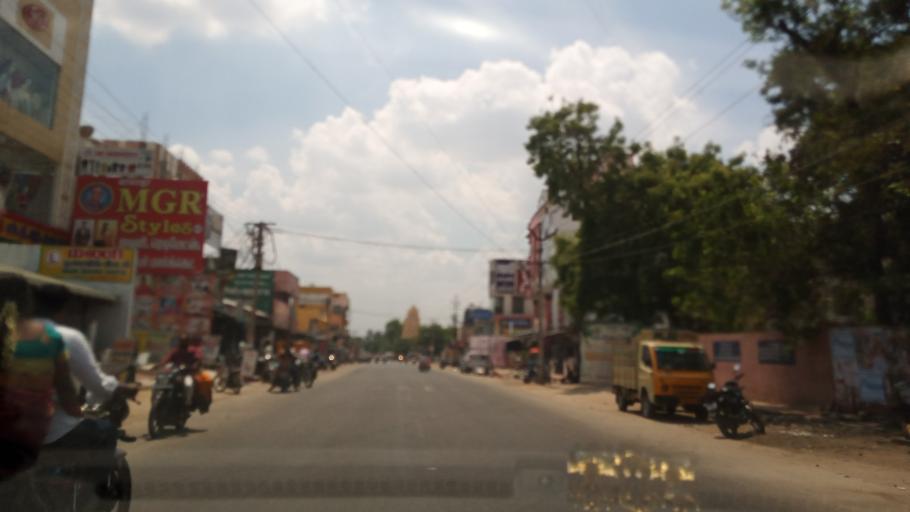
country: IN
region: Tamil Nadu
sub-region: Vellore
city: Walajapet
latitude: 12.9255
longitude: 79.3619
